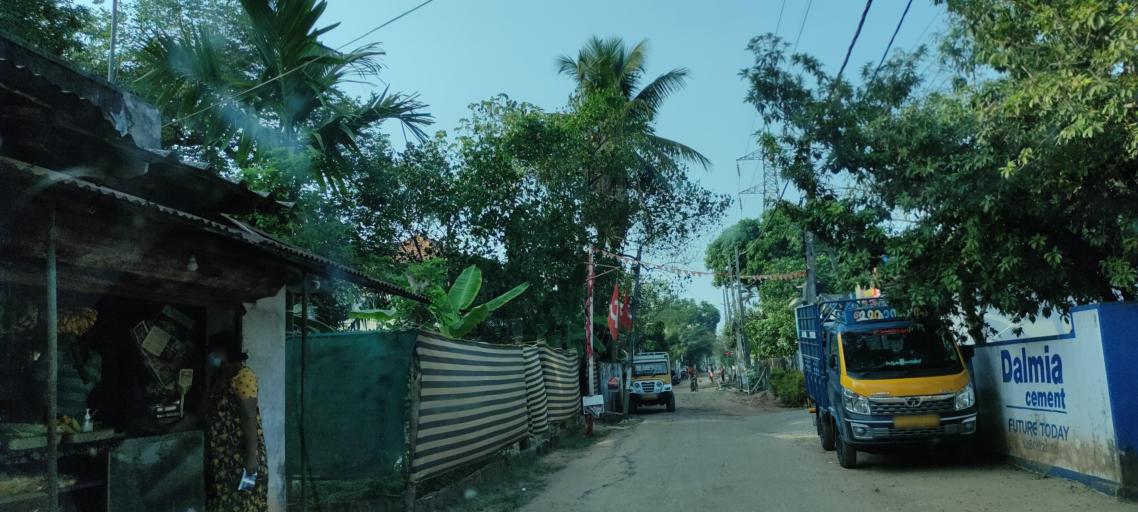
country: IN
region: Kerala
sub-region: Alappuzha
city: Alleppey
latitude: 9.5232
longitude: 76.3219
